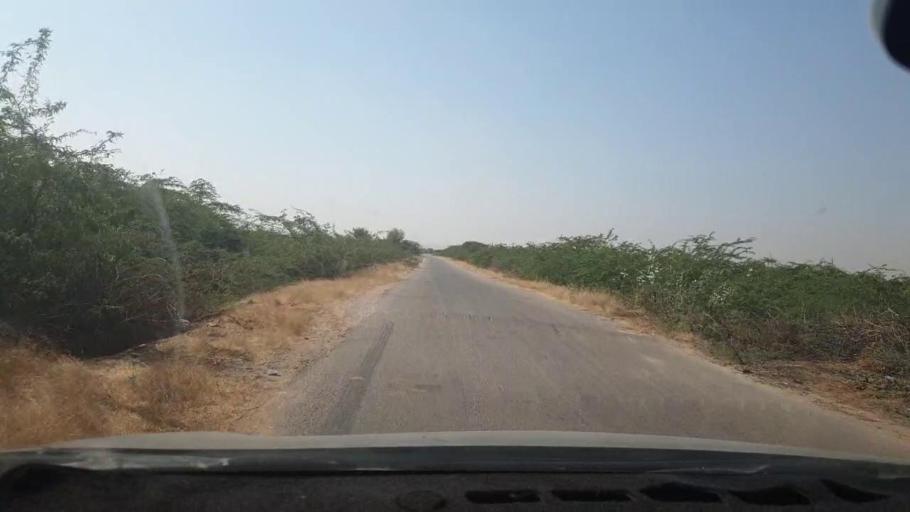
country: PK
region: Sindh
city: Malir Cantonment
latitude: 25.1579
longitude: 67.1494
